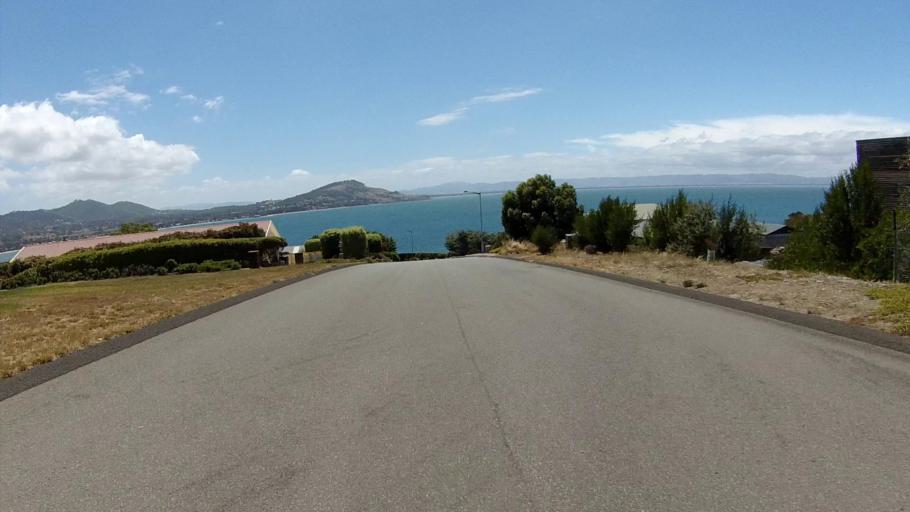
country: AU
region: Tasmania
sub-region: Clarence
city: Sandford
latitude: -42.9180
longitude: 147.5114
